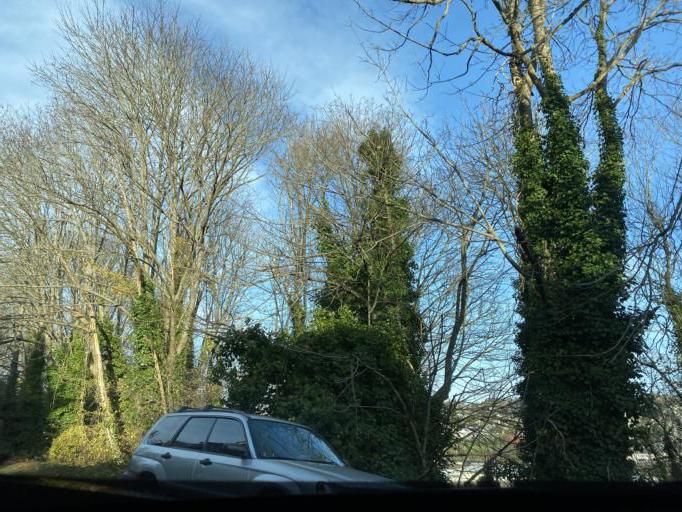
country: US
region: Washington
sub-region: King County
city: Seattle
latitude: 47.6384
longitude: -122.3862
